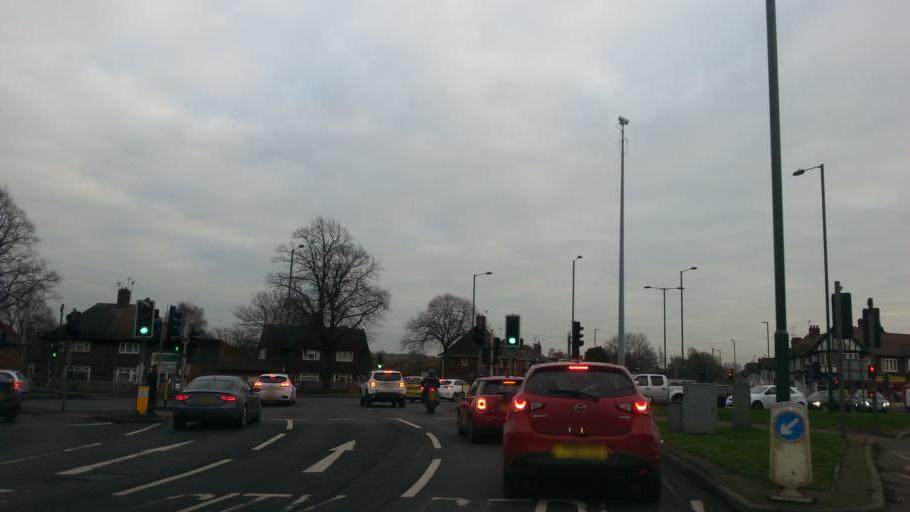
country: GB
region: England
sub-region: Nottingham
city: Nottingham
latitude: 52.9731
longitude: -1.1860
